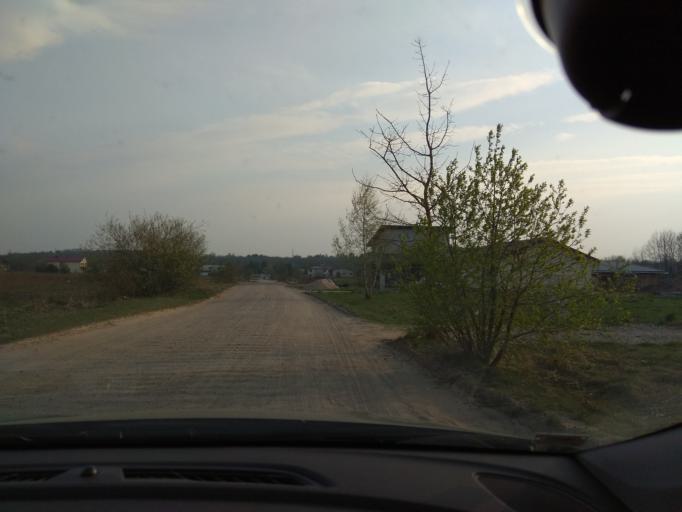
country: LT
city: Baltoji Voke
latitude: 54.5945
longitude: 25.1599
